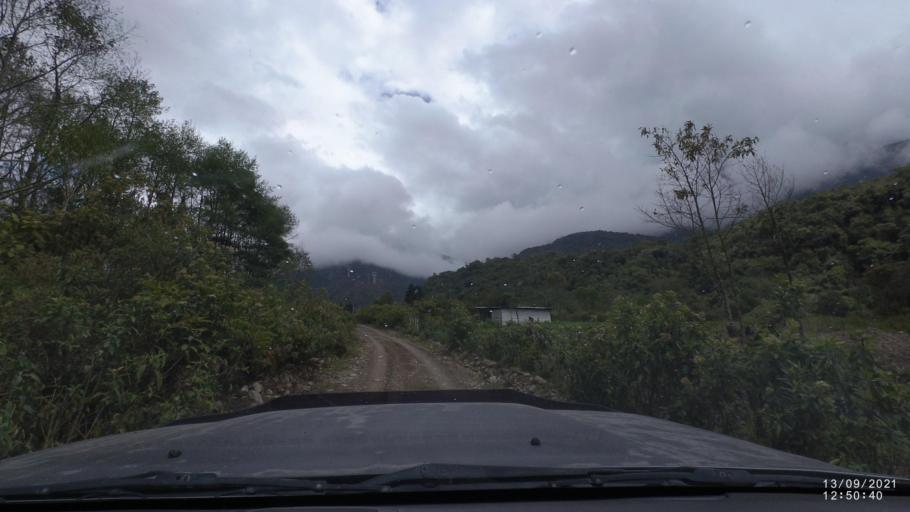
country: BO
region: Cochabamba
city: Colomi
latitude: -17.2376
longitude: -65.8195
